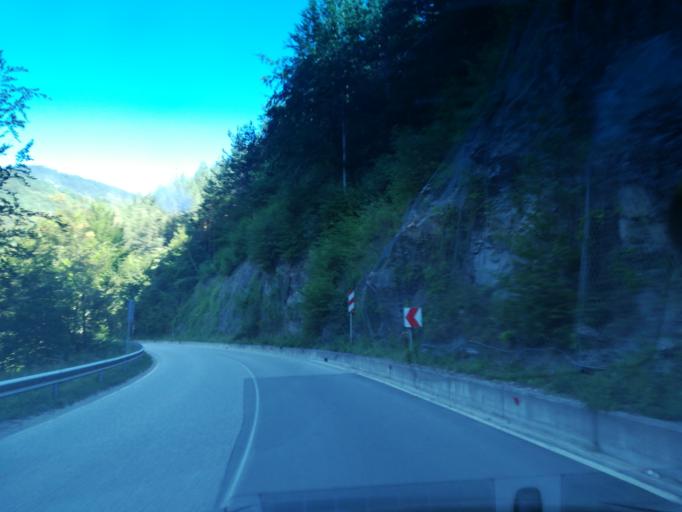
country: BG
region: Smolyan
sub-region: Obshtina Chepelare
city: Chepelare
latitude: 41.8183
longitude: 24.6966
